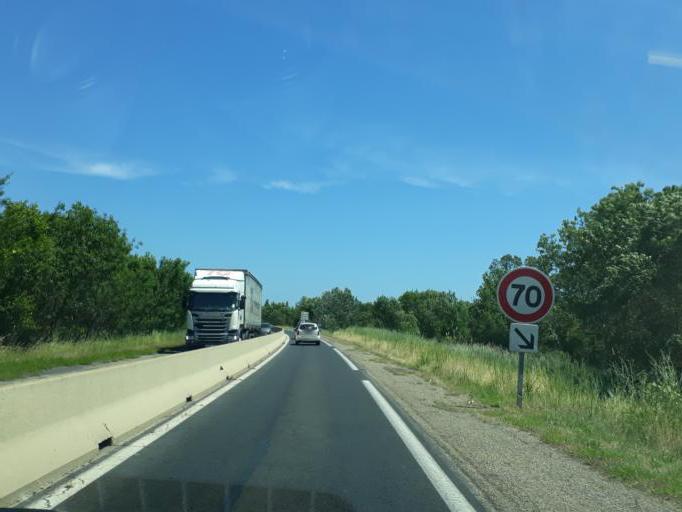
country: FR
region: Languedoc-Roussillon
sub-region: Departement de l'Herault
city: Vias
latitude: 43.3066
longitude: 3.4127
